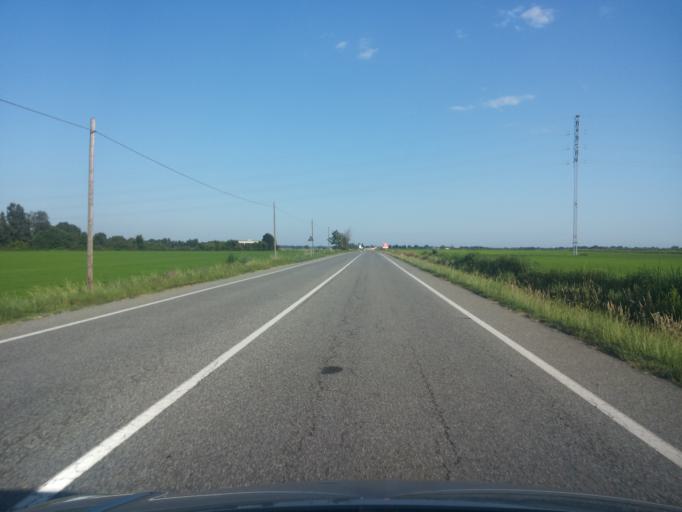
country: IT
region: Piedmont
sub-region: Provincia di Vercelli
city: Formigliana
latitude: 45.4213
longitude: 8.3059
